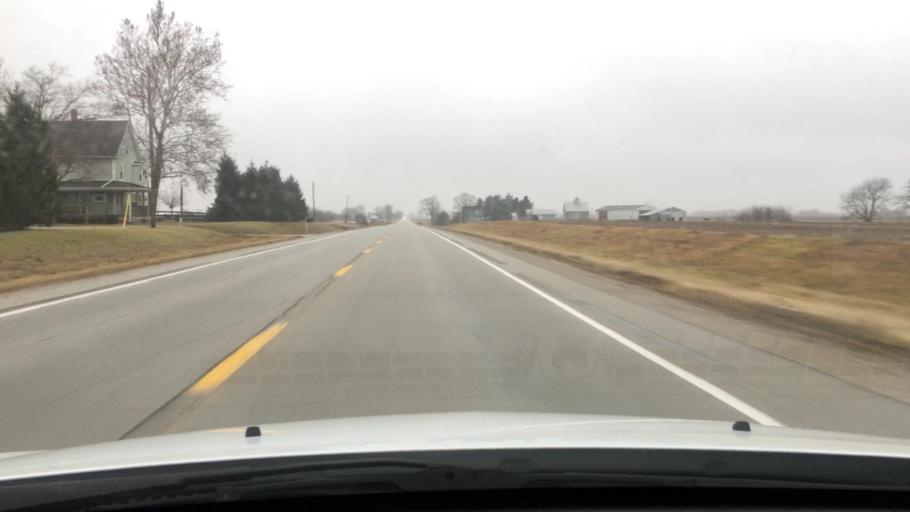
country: US
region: Illinois
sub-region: Livingston County
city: Pontiac
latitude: 40.8727
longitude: -88.7407
